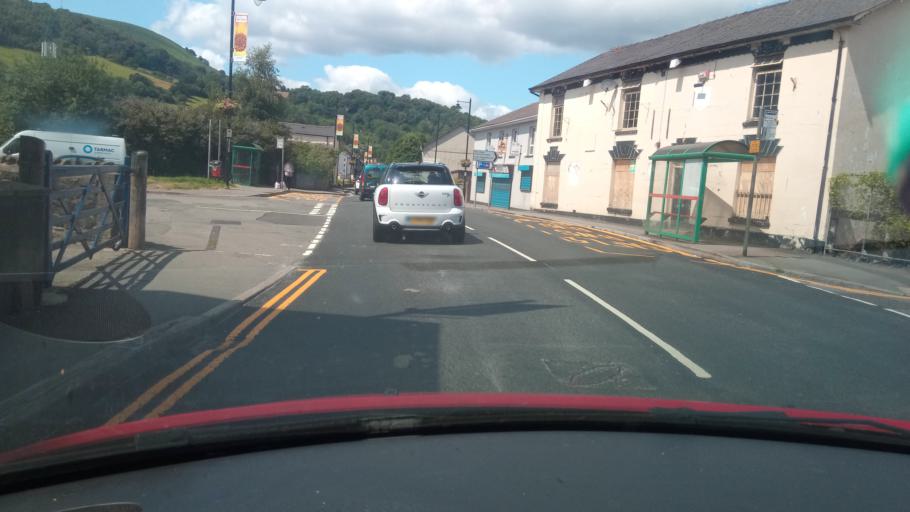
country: GB
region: Wales
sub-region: Caerphilly County Borough
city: Risca
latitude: 51.6034
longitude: -3.0931
